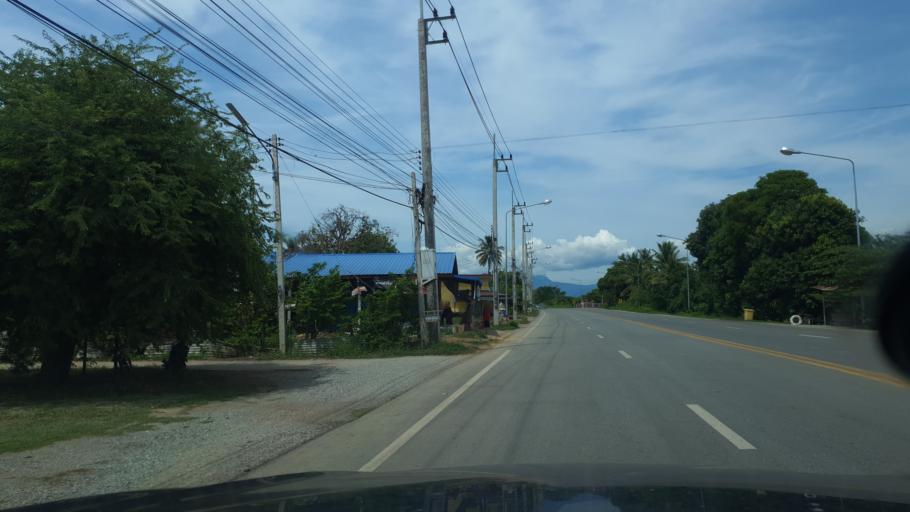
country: TH
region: Sukhothai
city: Sukhothai
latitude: 17.0524
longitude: 99.8190
